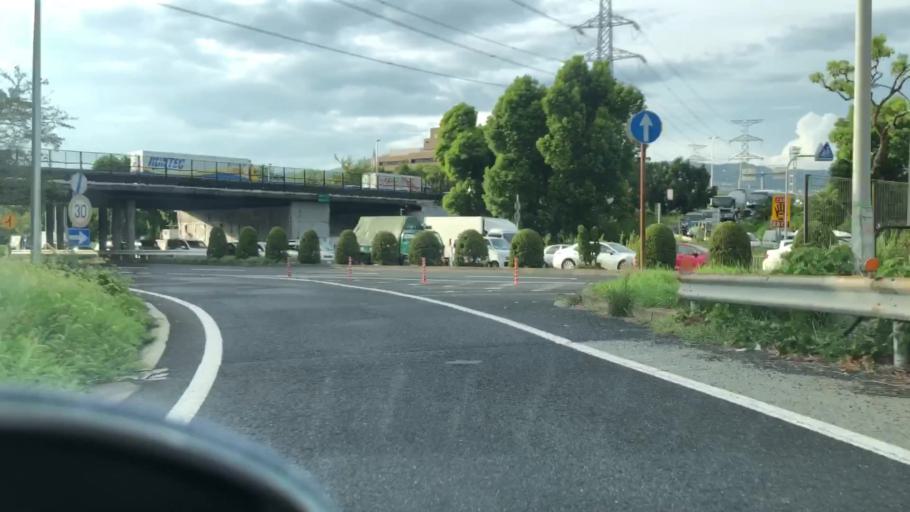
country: JP
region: Hyogo
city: Takarazuka
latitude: 34.8030
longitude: 135.3679
